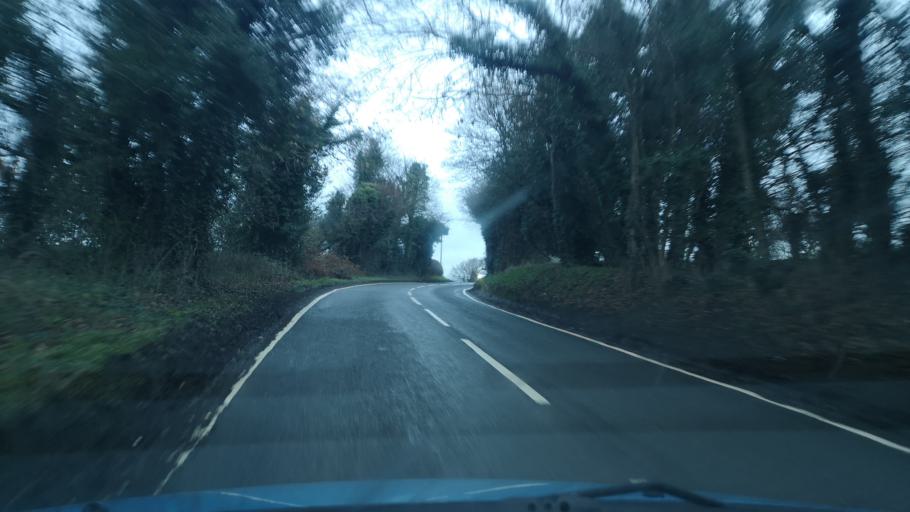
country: GB
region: England
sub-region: City and Borough of Wakefield
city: Ryhill
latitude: 53.6392
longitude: -1.4011
